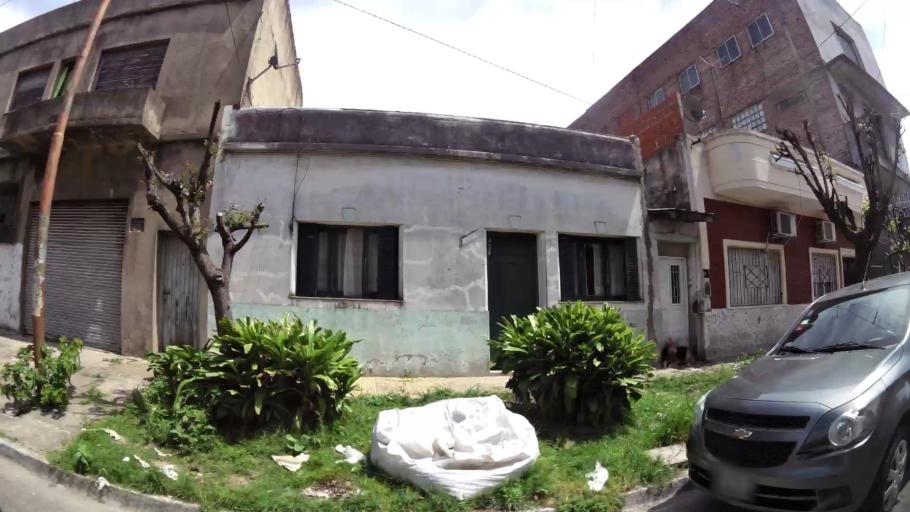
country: AR
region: Buenos Aires
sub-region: Partido de Lanus
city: Lanus
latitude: -34.6686
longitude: -58.4034
